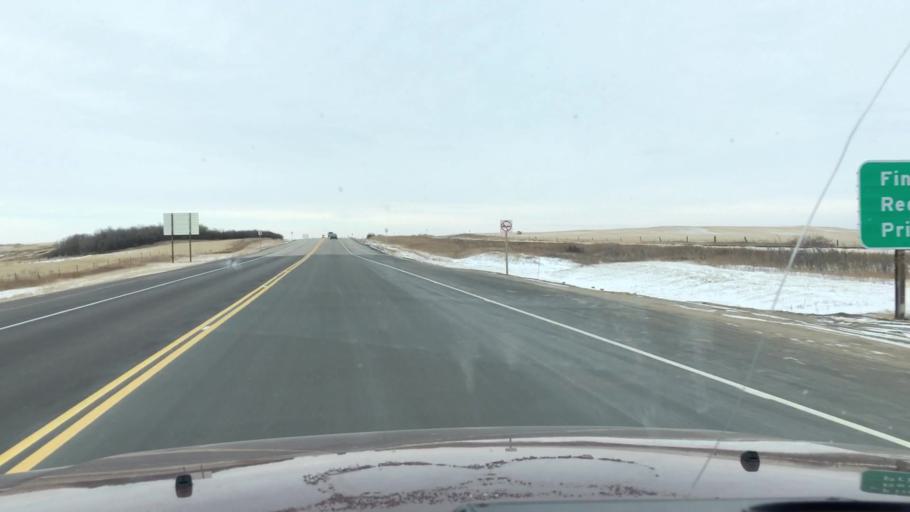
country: CA
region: Saskatchewan
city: Moose Jaw
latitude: 50.8476
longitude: -105.5609
